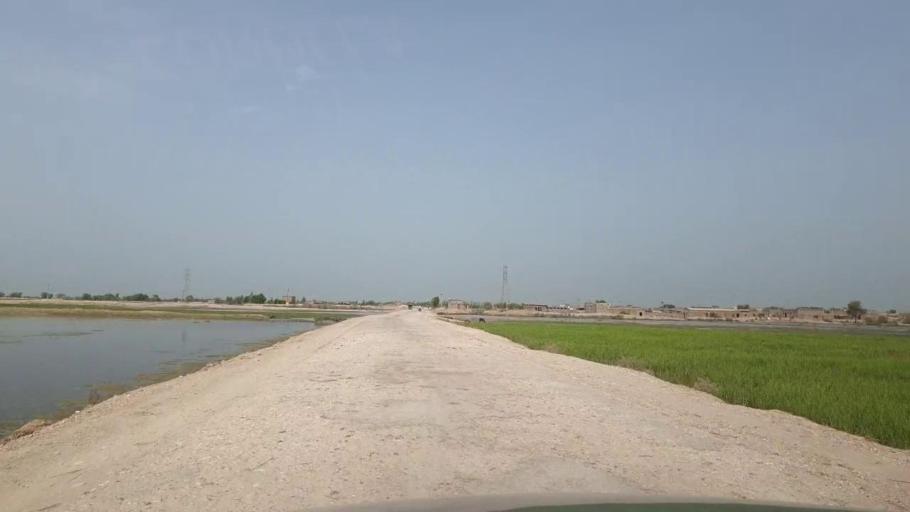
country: PK
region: Sindh
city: Garhi Yasin
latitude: 27.8544
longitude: 68.4298
